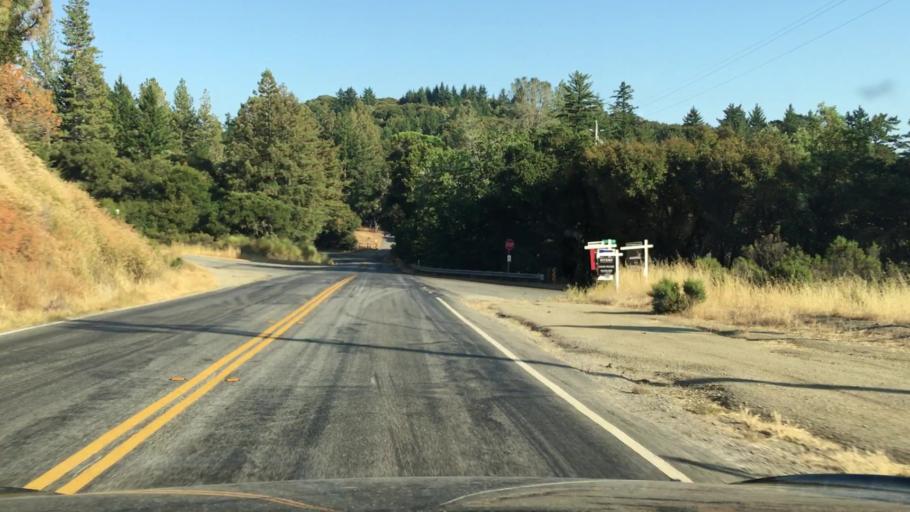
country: US
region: California
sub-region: Santa Clara County
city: Los Altos Hills
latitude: 37.3153
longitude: -122.1877
